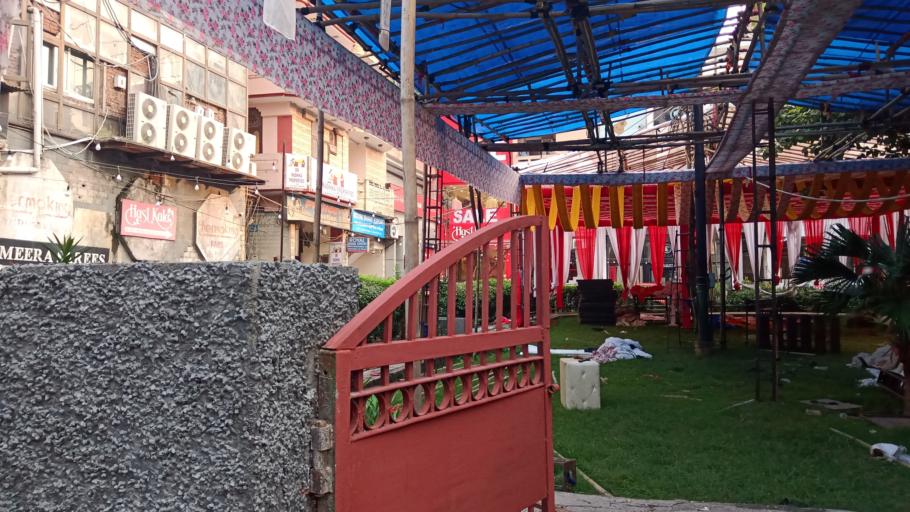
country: IN
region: NCT
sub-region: New Delhi
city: New Delhi
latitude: 28.5702
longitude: 77.2408
